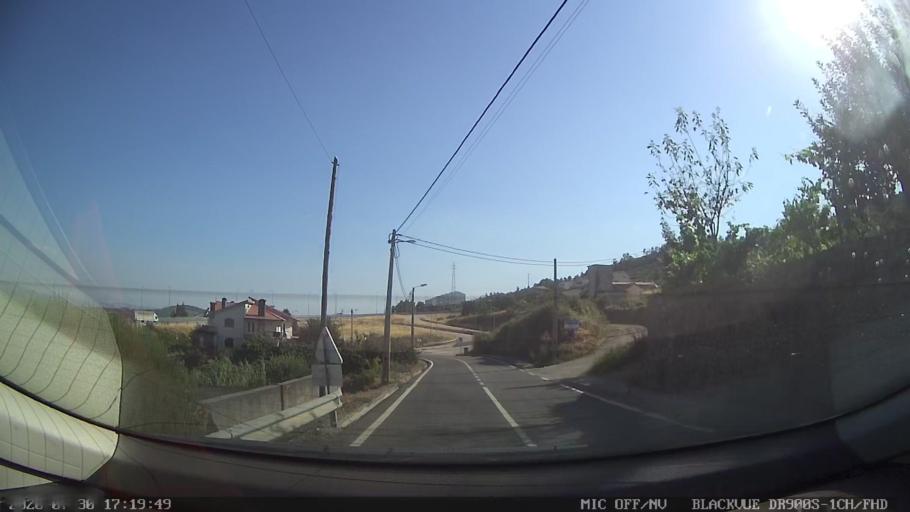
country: PT
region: Vila Real
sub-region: Sabrosa
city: Sabrosa
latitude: 41.2861
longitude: -7.4773
